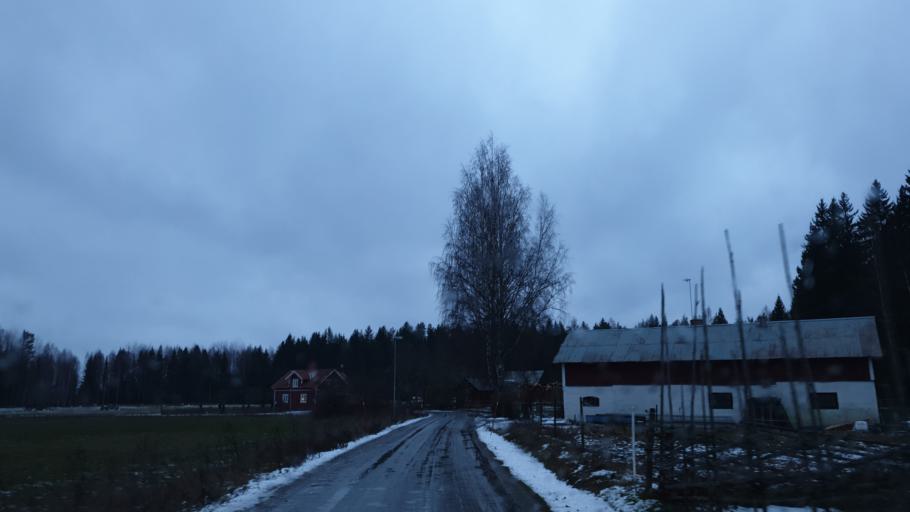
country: SE
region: Uppsala
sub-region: Tierps Kommun
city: Tierp
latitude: 60.3404
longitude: 17.4747
